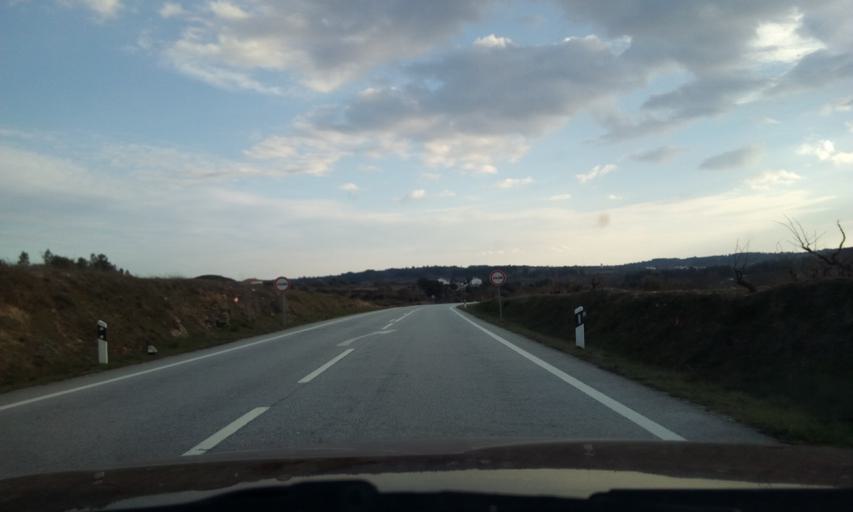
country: PT
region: Guarda
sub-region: Pinhel
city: Pinhel
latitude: 40.6774
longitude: -6.9501
